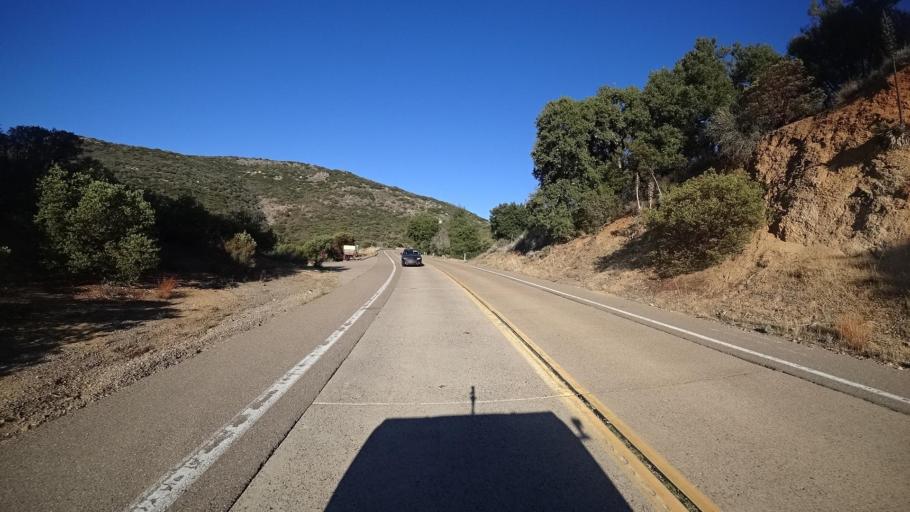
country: US
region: California
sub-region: San Diego County
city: Pine Valley
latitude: 32.8419
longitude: -116.5418
